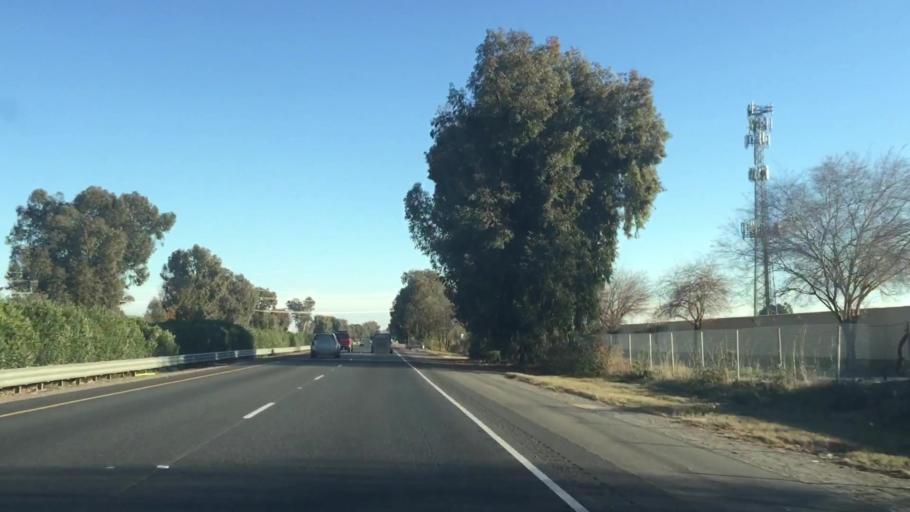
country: US
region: California
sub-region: Yuba County
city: Linda
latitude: 39.1187
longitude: -121.5678
